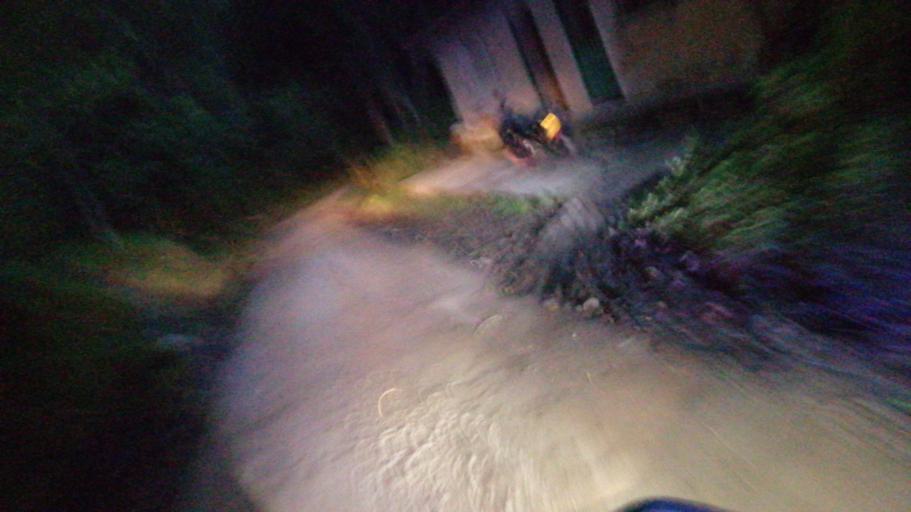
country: CO
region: Boyaca
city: Chinavita
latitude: 5.1469
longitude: -73.4033
